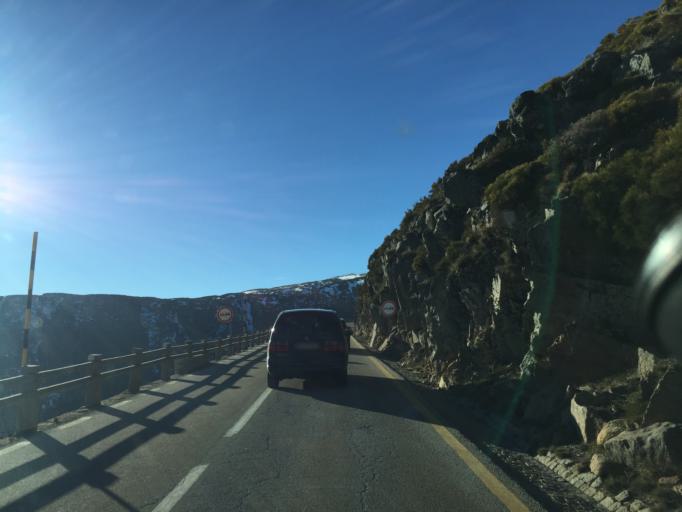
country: PT
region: Castelo Branco
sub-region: Covilha
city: Covilha
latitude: 40.3188
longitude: -7.5948
